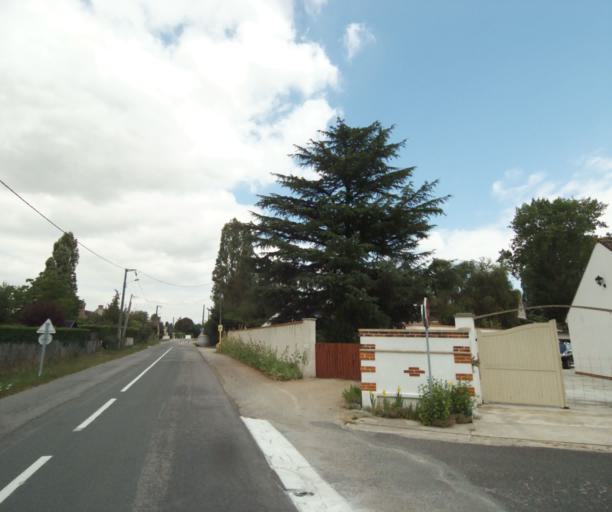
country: FR
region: Centre
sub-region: Departement du Loiret
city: Checy
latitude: 47.9155
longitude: 2.0401
